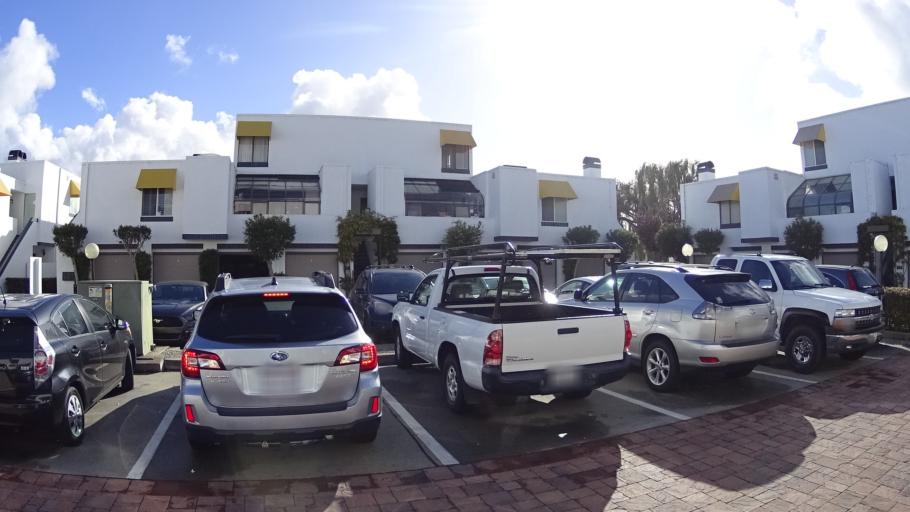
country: US
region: California
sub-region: San Mateo County
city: Foster City
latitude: 37.5542
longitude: -122.2692
